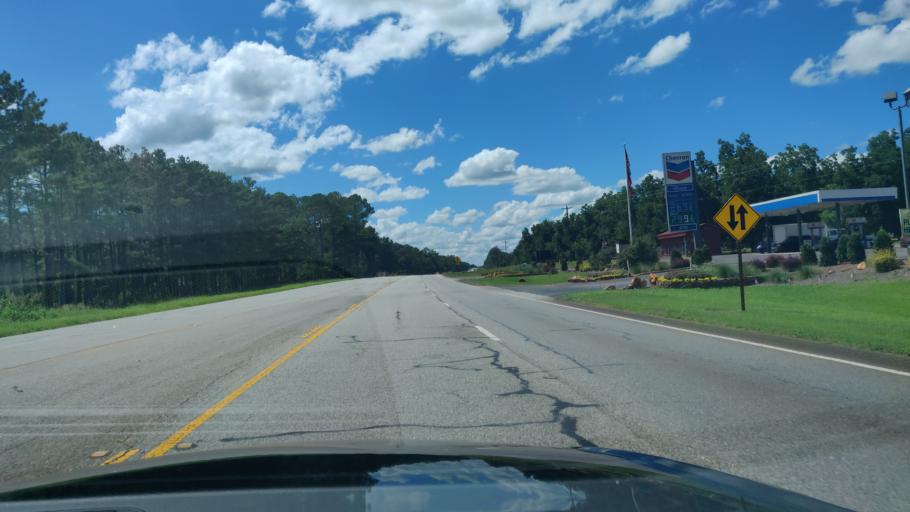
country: US
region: Georgia
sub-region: Webster County
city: Preston
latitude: 31.9686
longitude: -84.6050
